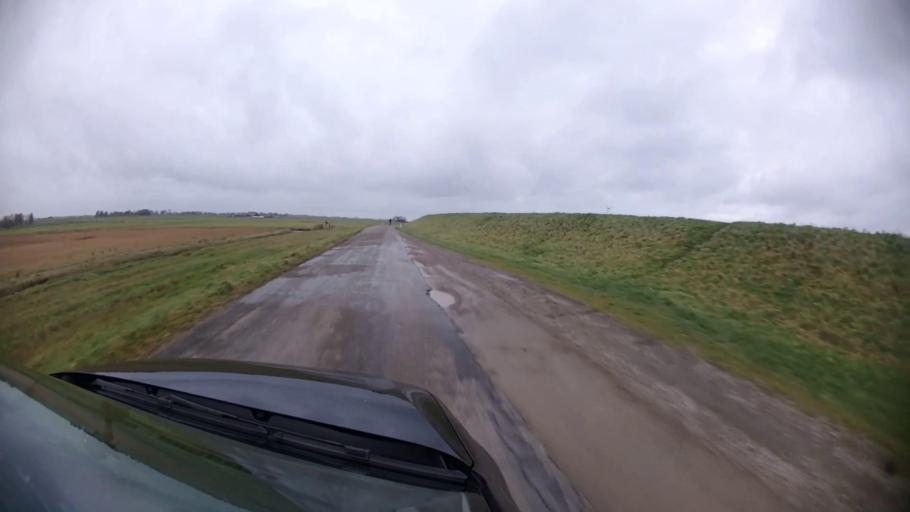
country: NL
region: North Holland
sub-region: Gemeente Waterland
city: Broek in Waterland
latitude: 52.4004
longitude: 5.0308
